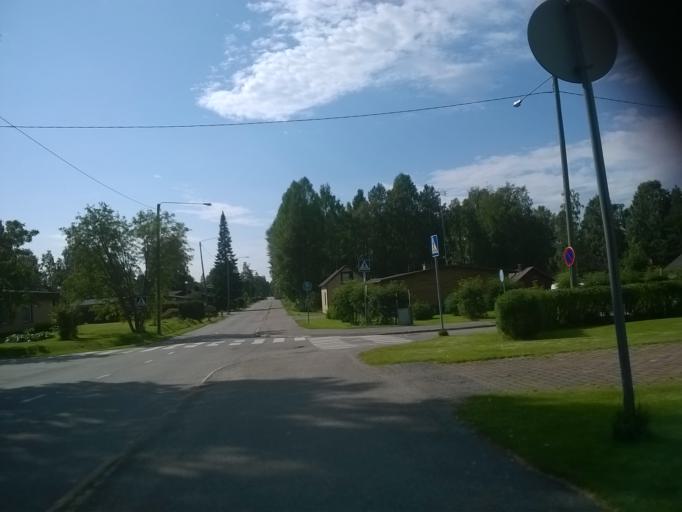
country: FI
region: Kainuu
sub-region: Kehys-Kainuu
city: Kuhmo
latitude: 64.1280
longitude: 29.5314
